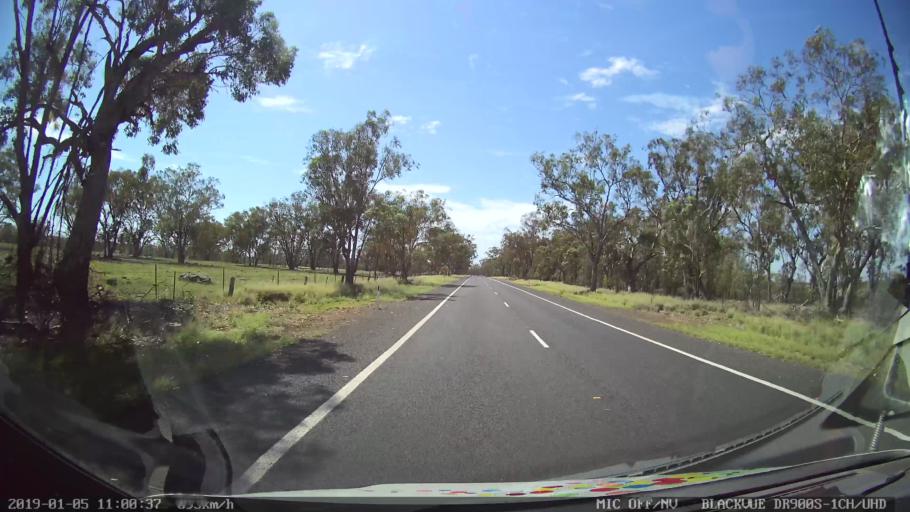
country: AU
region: New South Wales
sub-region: Warrumbungle Shire
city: Coonabarabran
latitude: -31.4191
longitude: 149.2142
